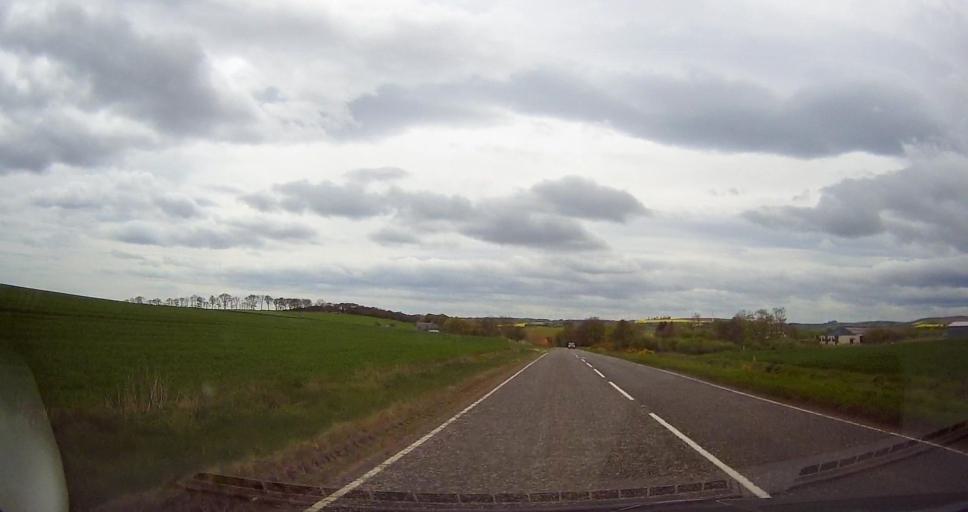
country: GB
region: Scotland
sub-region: Aberdeenshire
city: Stonehaven
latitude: 56.9149
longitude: -2.2146
